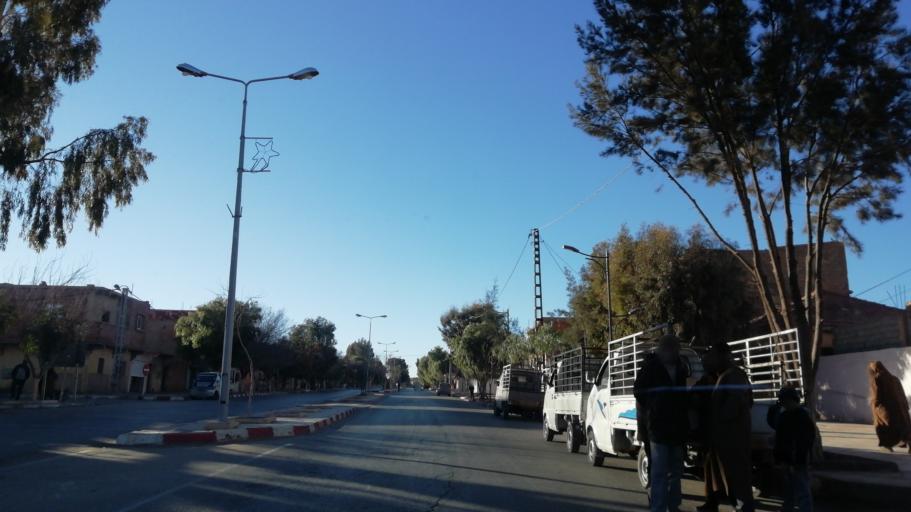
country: DZ
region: Saida
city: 'Ain el Hadjar
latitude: 34.0401
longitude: 0.0871
